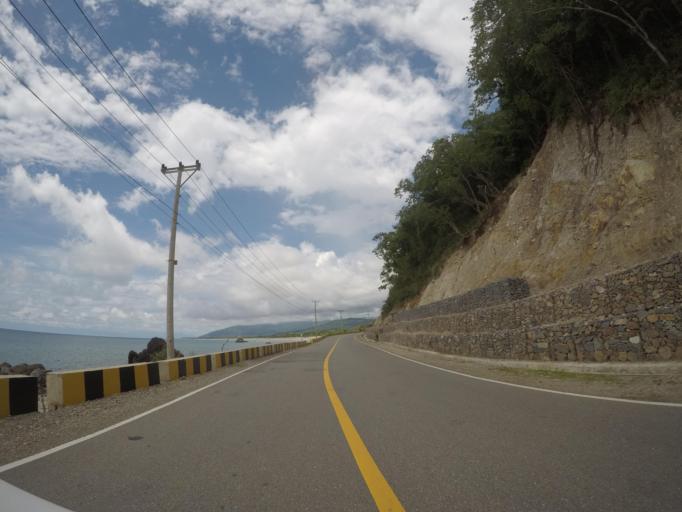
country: TL
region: Liquica
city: Maubara
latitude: -8.7999
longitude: 125.0947
